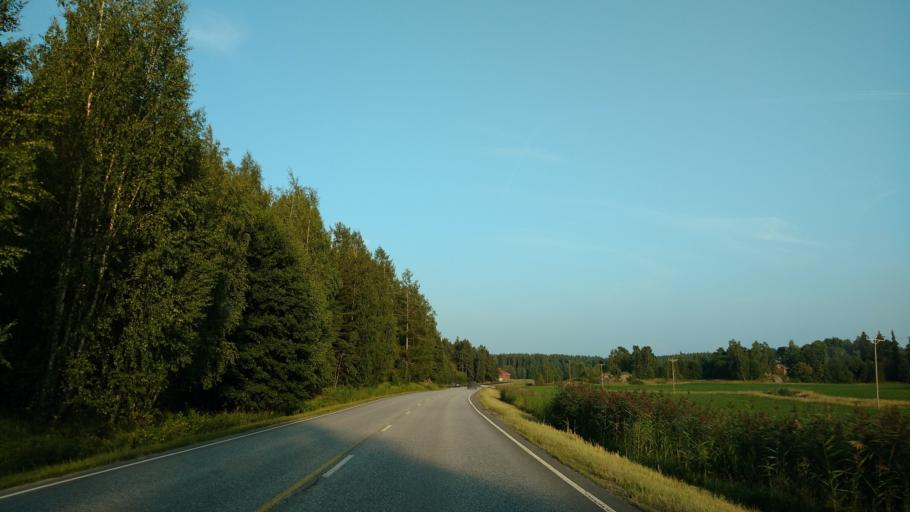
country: FI
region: Varsinais-Suomi
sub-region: Salo
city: Saerkisalo
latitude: 60.1872
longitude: 22.8883
